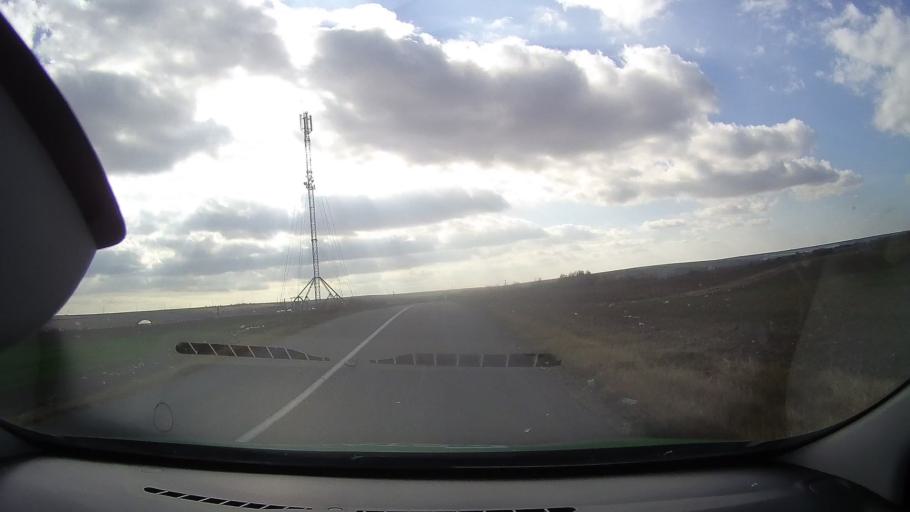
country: RO
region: Constanta
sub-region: Comuna Sacele
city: Sacele
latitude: 44.4926
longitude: 28.6547
